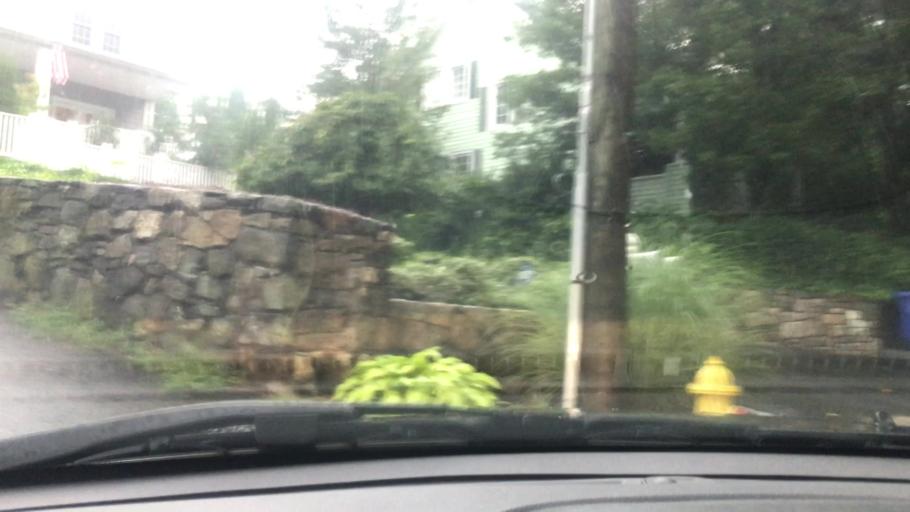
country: US
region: Connecticut
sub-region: Fairfield County
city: Norwalk
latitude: 41.0923
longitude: -73.4315
